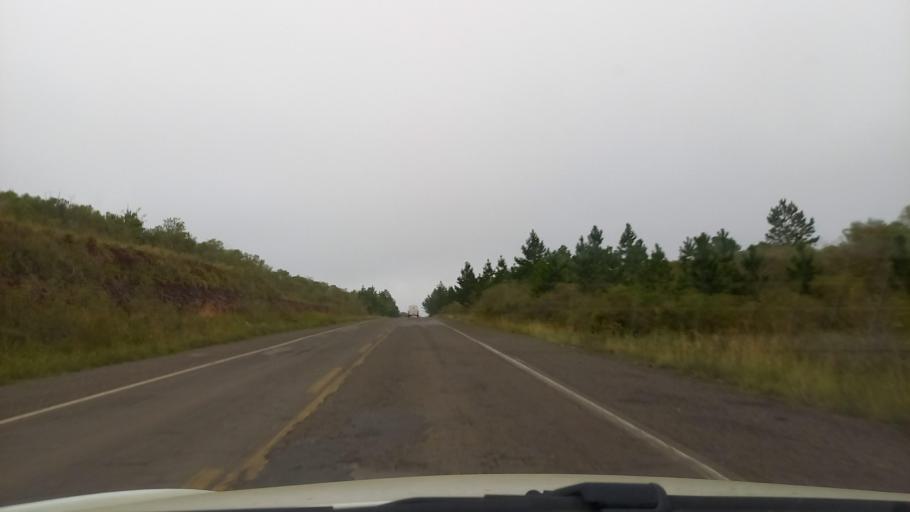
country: BR
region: Rio Grande do Sul
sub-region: Cacequi
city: Cacequi
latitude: -30.0847
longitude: -54.6236
